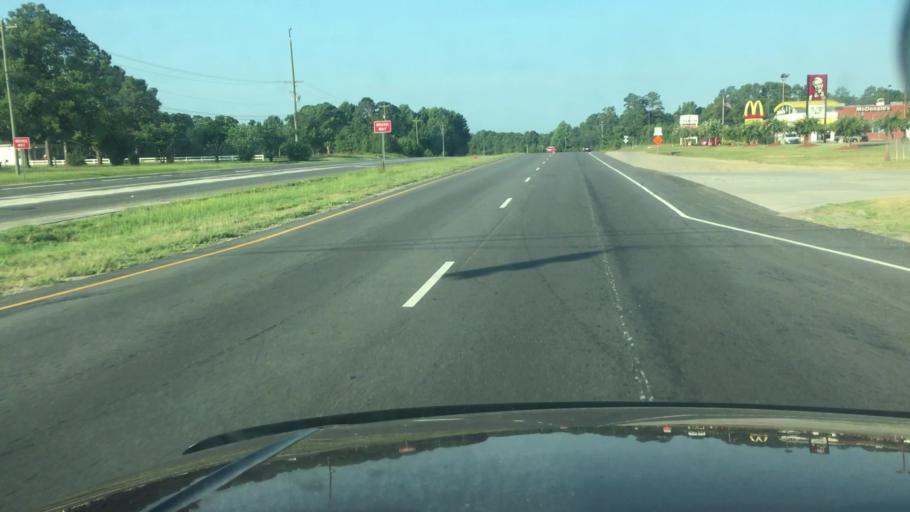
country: US
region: North Carolina
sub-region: Cumberland County
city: Hope Mills
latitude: 34.9301
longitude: -78.8538
